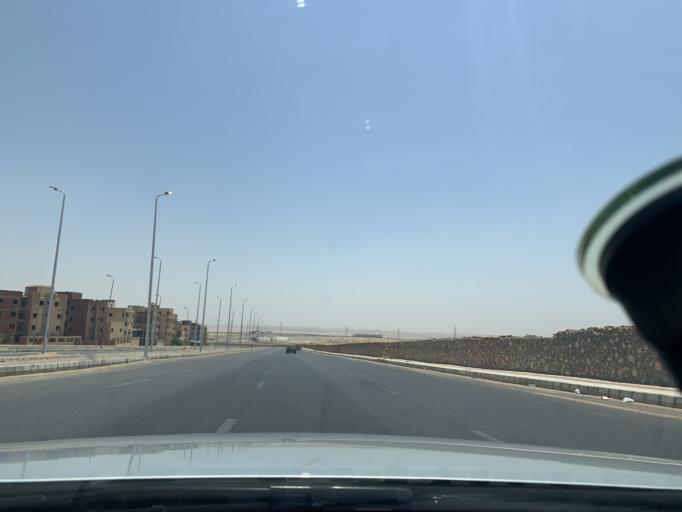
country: EG
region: Muhafazat al Qahirah
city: Halwan
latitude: 29.9828
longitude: 31.4686
